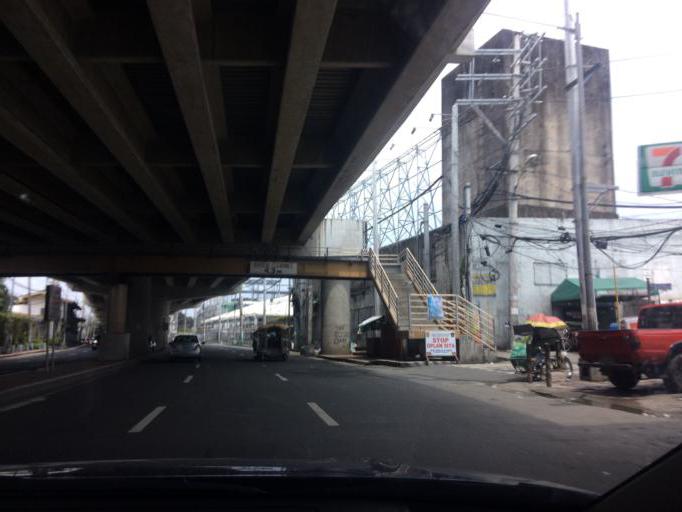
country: PH
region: Metro Manila
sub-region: Makati City
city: Makati City
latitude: 14.5270
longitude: 121.0103
